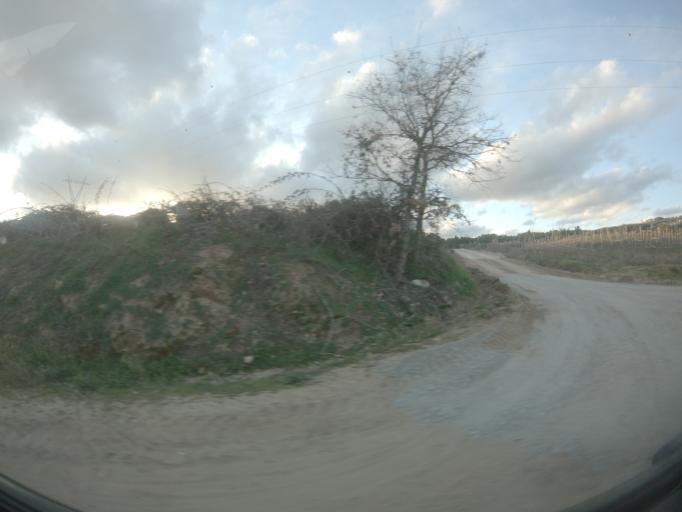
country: PT
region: Braganca
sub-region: Carrazeda de Ansiaes
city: Carrazeda de Anciaes
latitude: 41.2191
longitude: -7.3180
